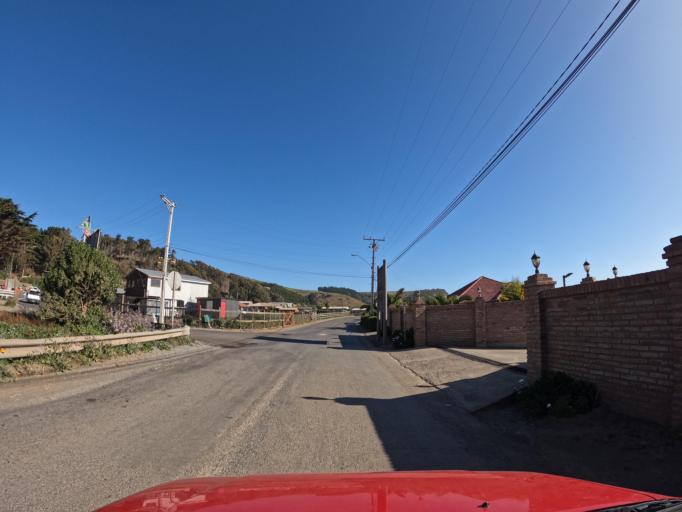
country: CL
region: Maule
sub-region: Provincia de Talca
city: Constitucion
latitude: -34.8512
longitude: -72.1415
